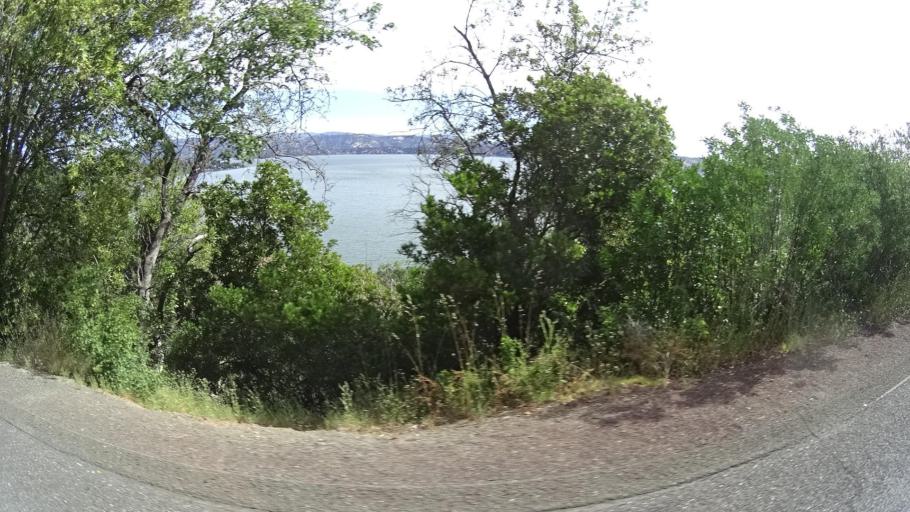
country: US
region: California
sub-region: Lake County
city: Soda Bay
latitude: 38.9629
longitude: -122.7342
